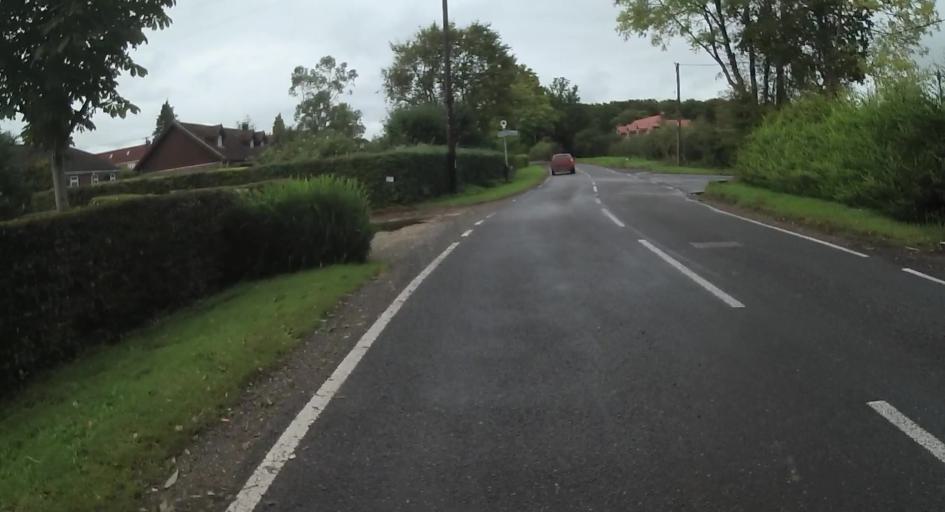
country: GB
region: England
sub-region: Hampshire
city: Tadley
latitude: 51.3440
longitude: -1.1632
